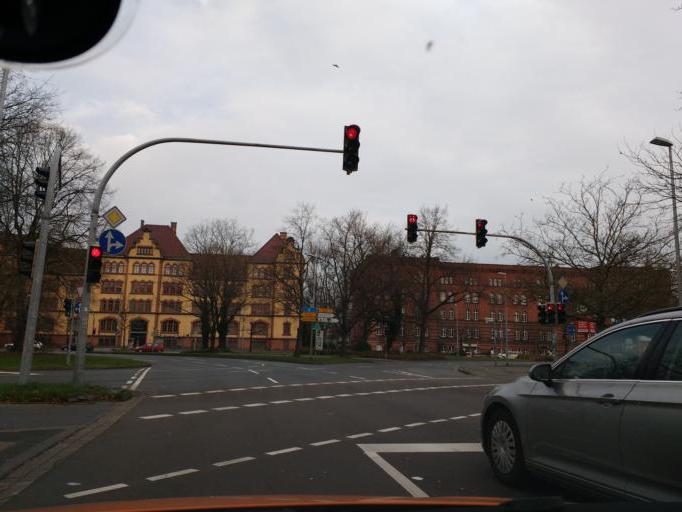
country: DE
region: Lower Saxony
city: Oldenburg
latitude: 53.1458
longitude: 8.2149
